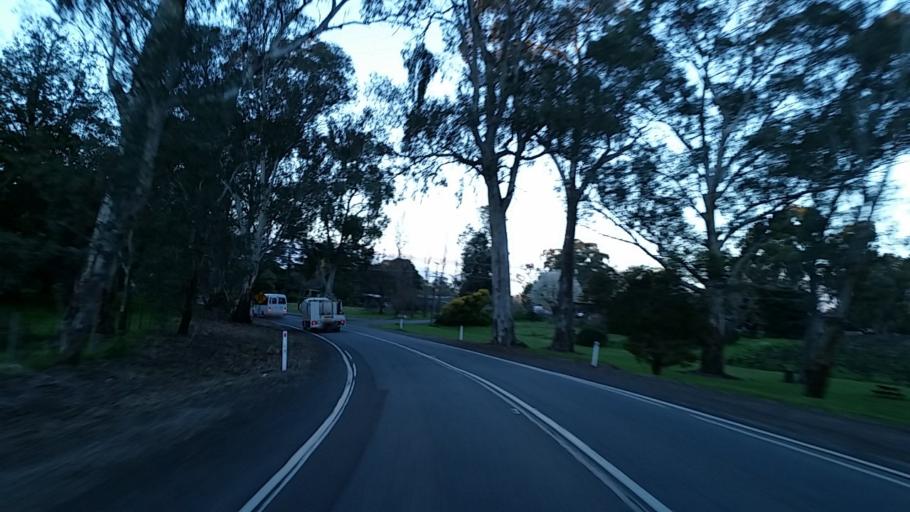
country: AU
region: South Australia
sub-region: Barossa
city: Williamstown
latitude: -34.6791
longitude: 138.8843
